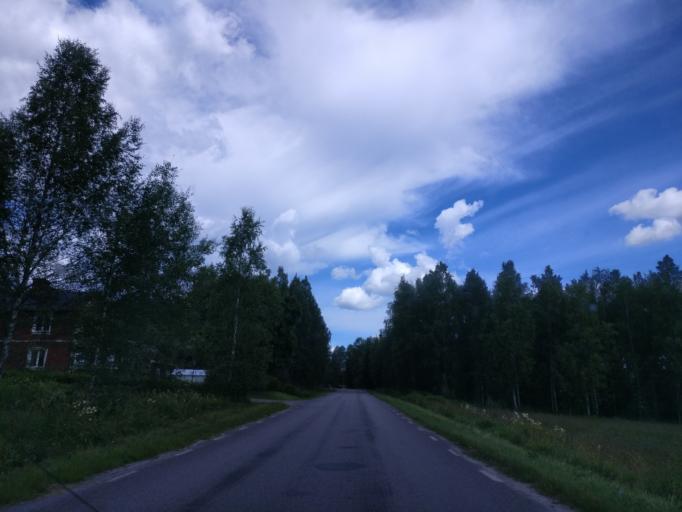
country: SE
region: Vaermland
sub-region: Hagfors Kommun
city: Ekshaerad
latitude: 60.1357
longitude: 13.4585
